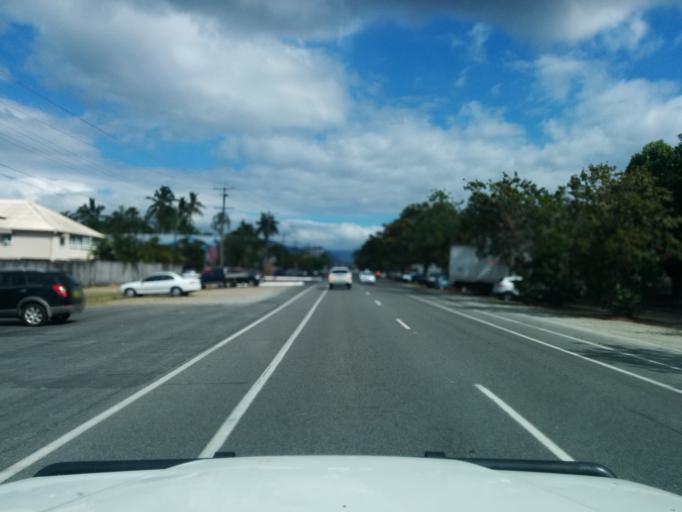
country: AU
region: Queensland
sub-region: Cairns
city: Cairns
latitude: -16.9154
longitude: 145.7650
